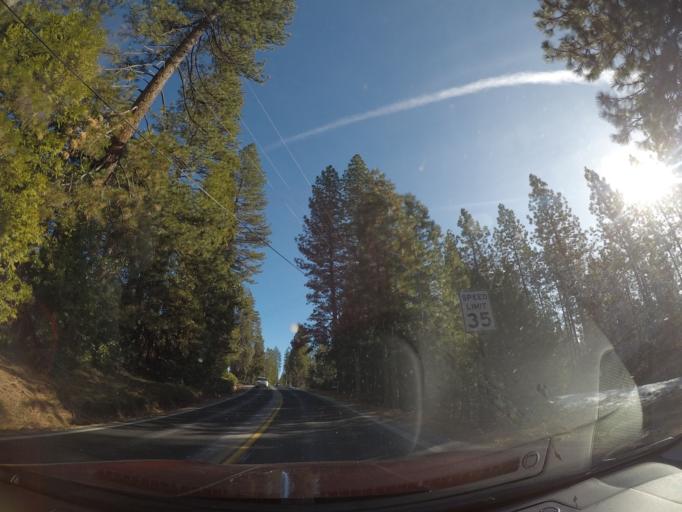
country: US
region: California
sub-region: Tuolumne County
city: Twain Harte
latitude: 38.0665
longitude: -120.1860
